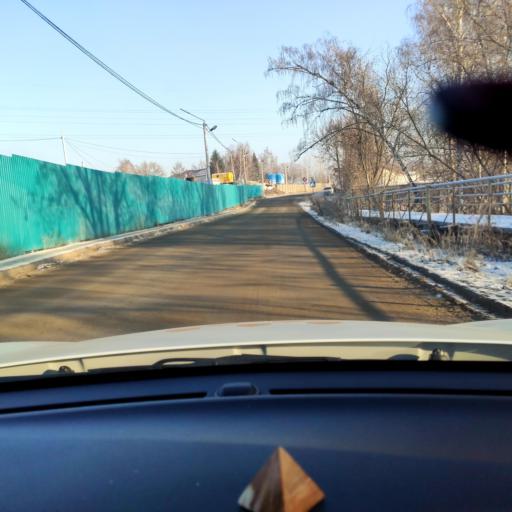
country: RU
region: Tatarstan
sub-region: Gorod Kazan'
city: Kazan
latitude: 55.8126
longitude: 49.0497
